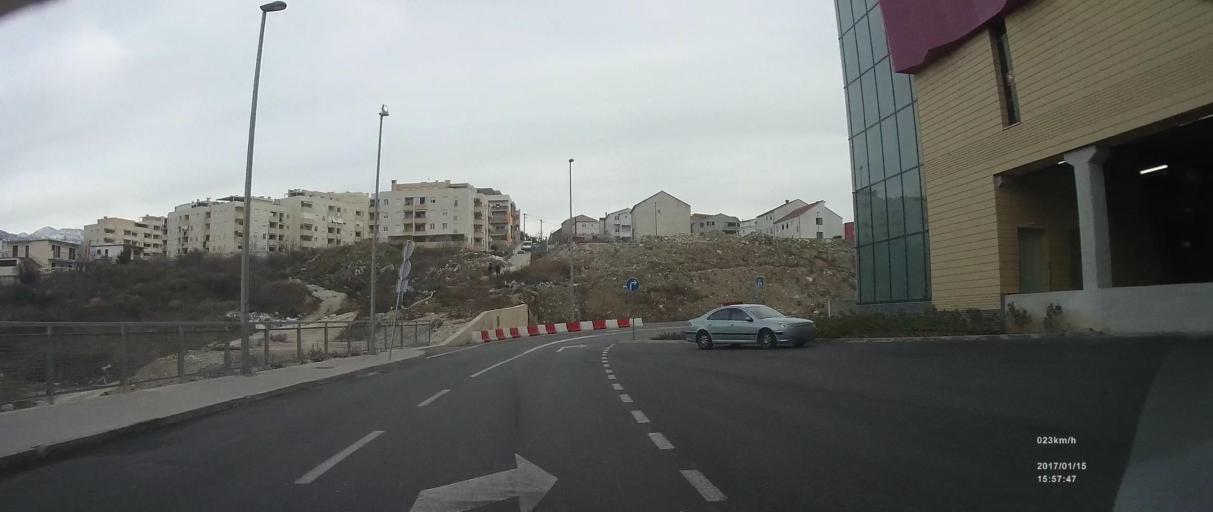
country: HR
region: Splitsko-Dalmatinska
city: Vranjic
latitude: 43.5196
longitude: 16.4852
